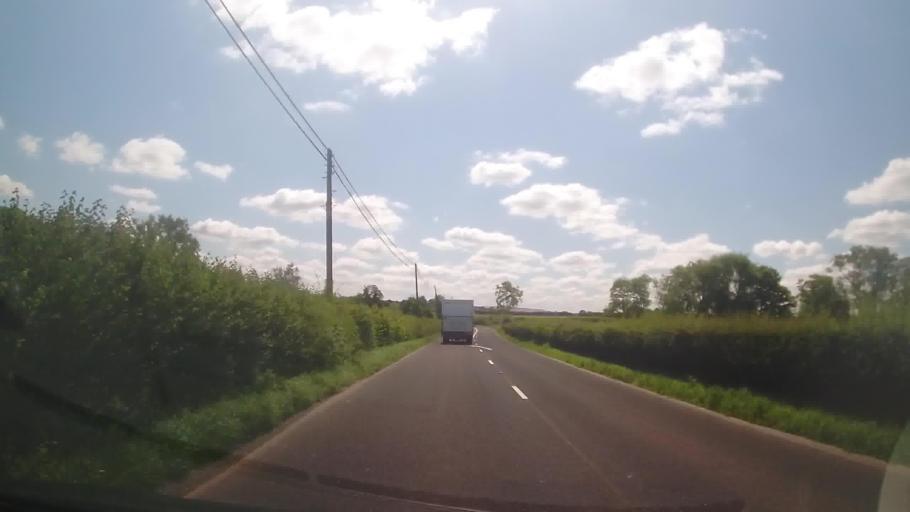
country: GB
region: England
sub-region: Herefordshire
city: Ocle Pychard
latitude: 52.1289
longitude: -2.6027
